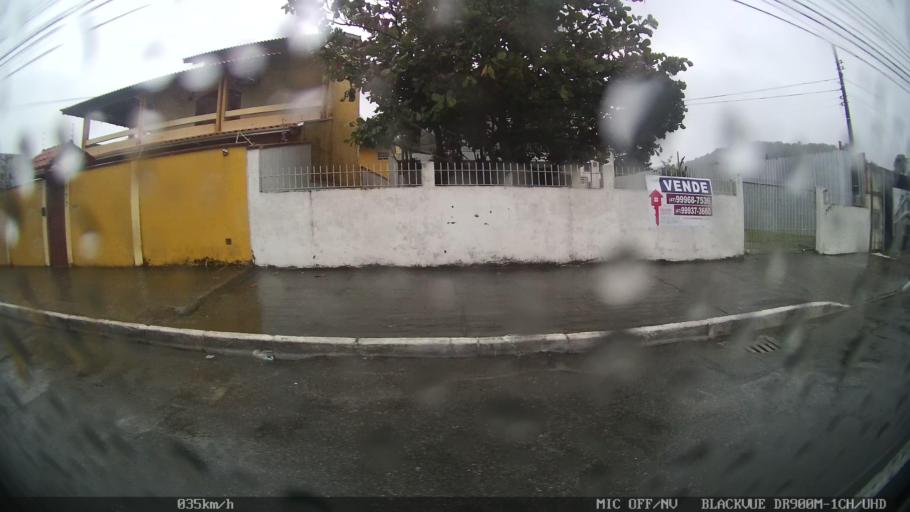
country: BR
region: Santa Catarina
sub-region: Balneario Camboriu
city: Balneario Camboriu
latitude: -26.9558
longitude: -48.6373
